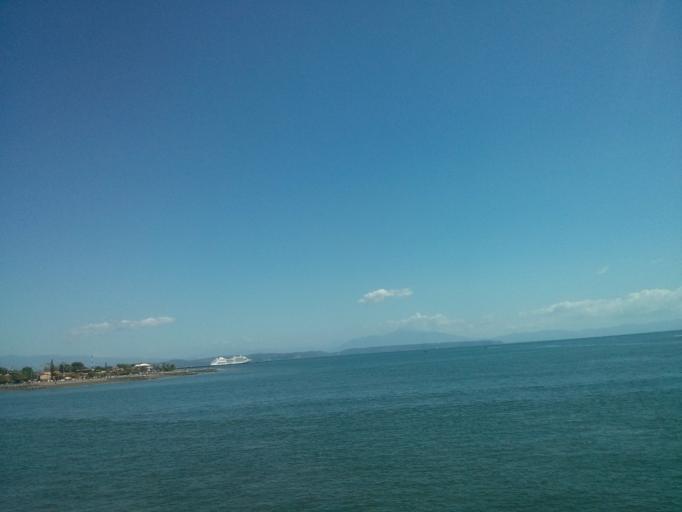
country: CR
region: Puntarenas
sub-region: Canton Central de Puntarenas
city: Puntarenas
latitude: 9.9751
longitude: -84.8553
